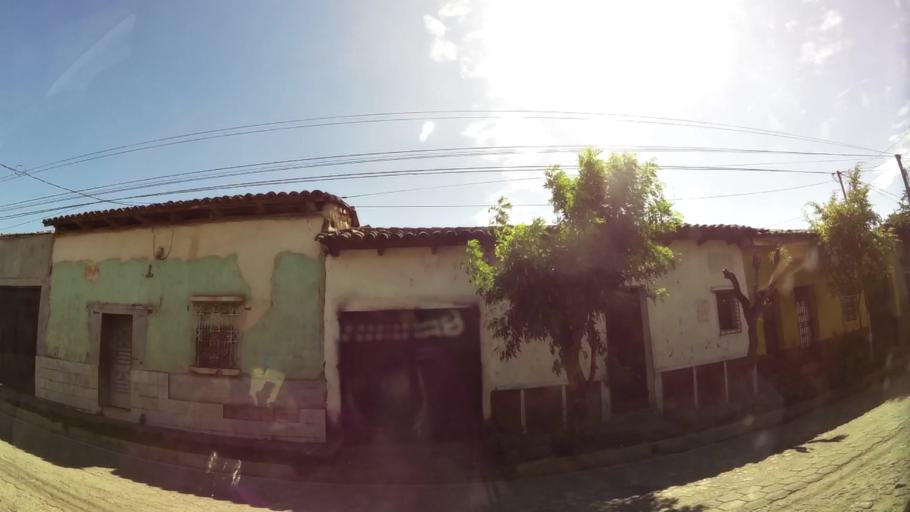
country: SV
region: Santa Ana
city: Chalchuapa
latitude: 13.9878
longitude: -89.6772
